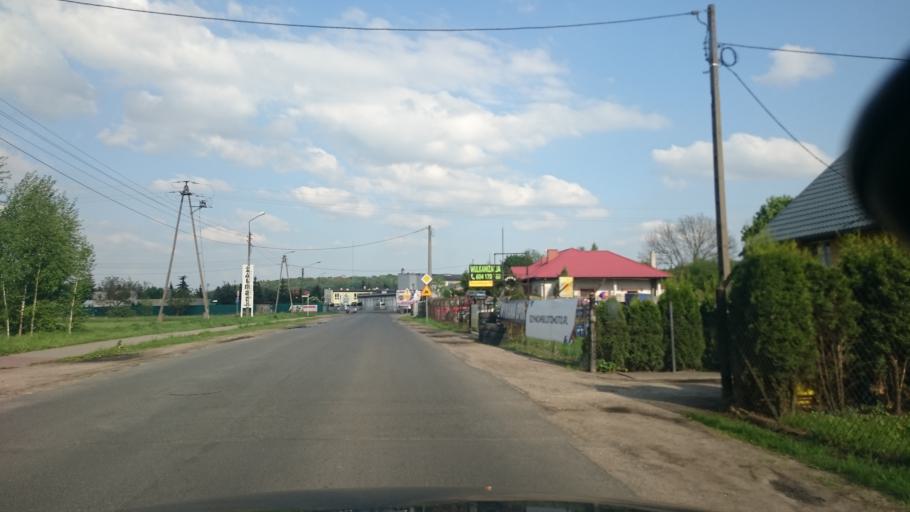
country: PL
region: Kujawsko-Pomorskie
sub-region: Grudziadz
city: Grudziadz
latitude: 53.4868
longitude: 18.8079
